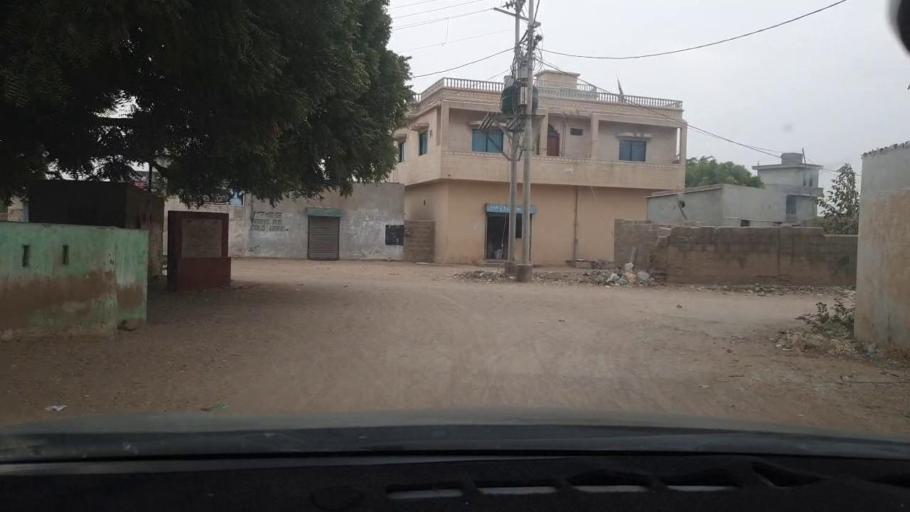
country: PK
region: Sindh
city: Malir Cantonment
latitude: 24.9213
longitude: 67.3187
